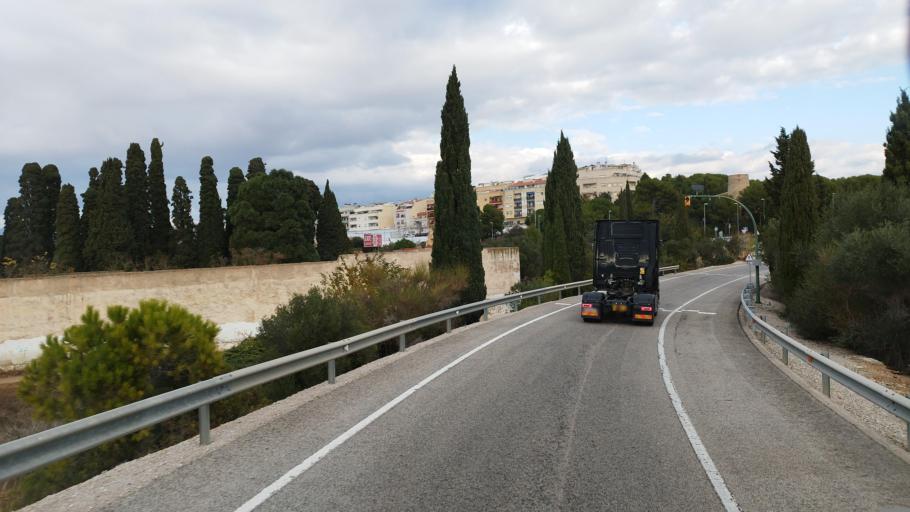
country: ES
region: Catalonia
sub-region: Provincia de Tarragona
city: El Vendrell
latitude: 41.2178
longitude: 1.5433
